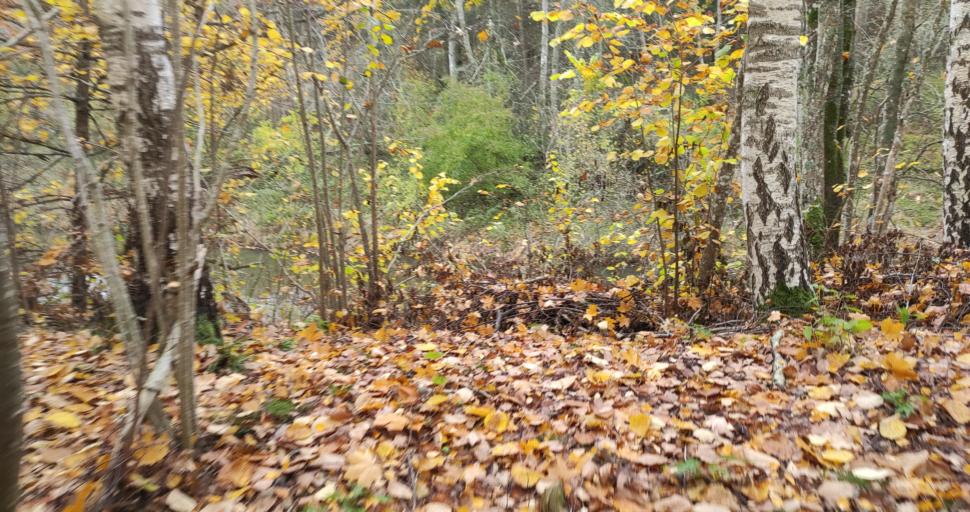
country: LV
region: Durbe
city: Liegi
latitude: 56.7491
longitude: 21.3416
